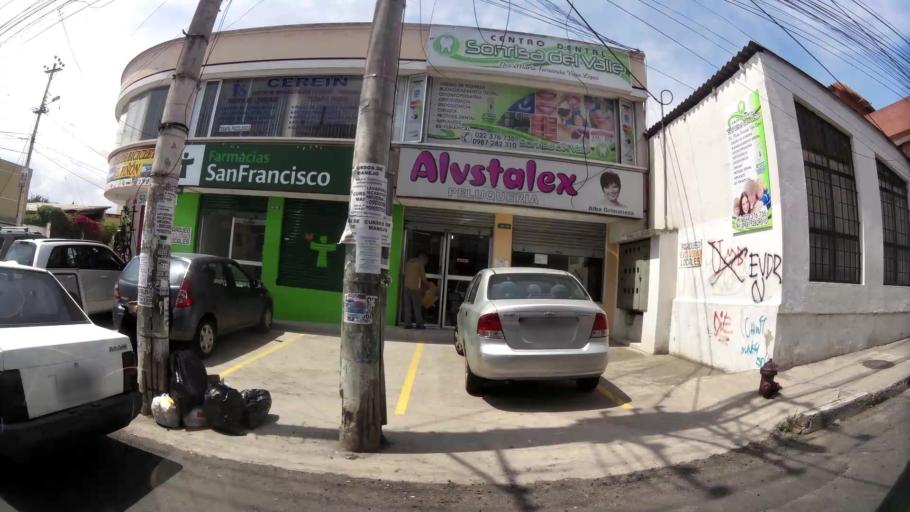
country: EC
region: Pichincha
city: Quito
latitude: -0.2118
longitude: -78.4029
